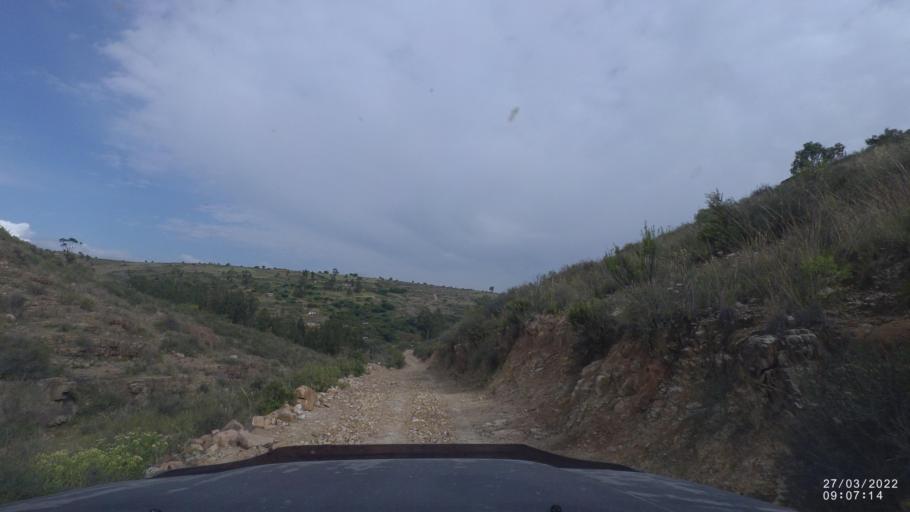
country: BO
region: Cochabamba
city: Cliza
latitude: -17.7324
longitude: -65.8717
